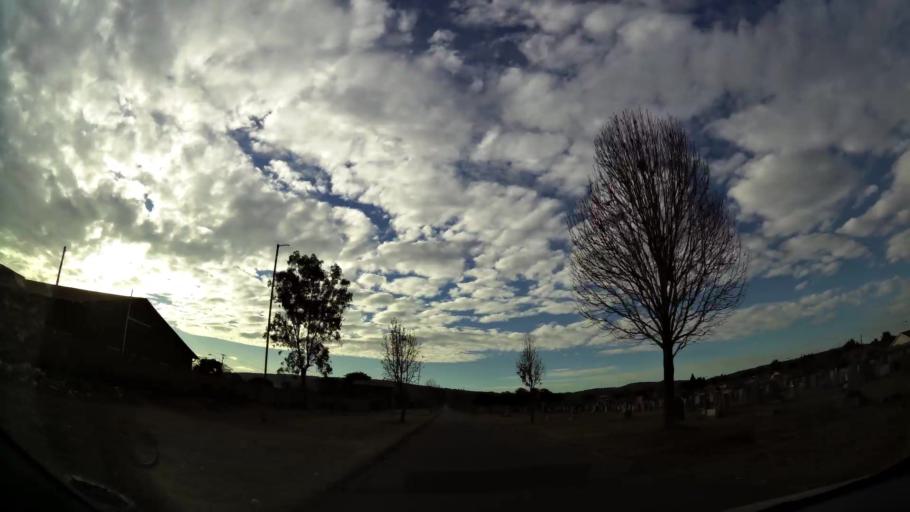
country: ZA
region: Gauteng
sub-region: City of Tshwane Metropolitan Municipality
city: Pretoria
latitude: -25.7099
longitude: 28.3250
